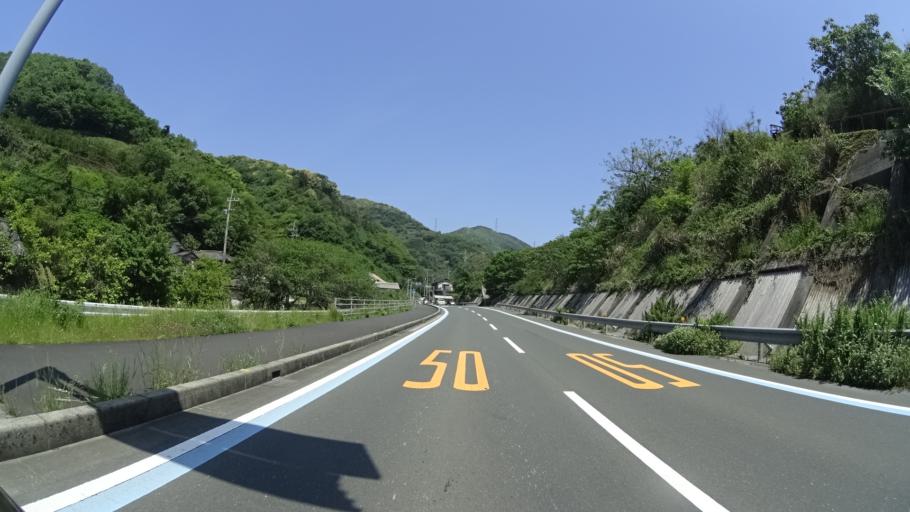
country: JP
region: Ehime
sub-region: Nishiuwa-gun
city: Ikata-cho
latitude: 33.4987
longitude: 132.3971
